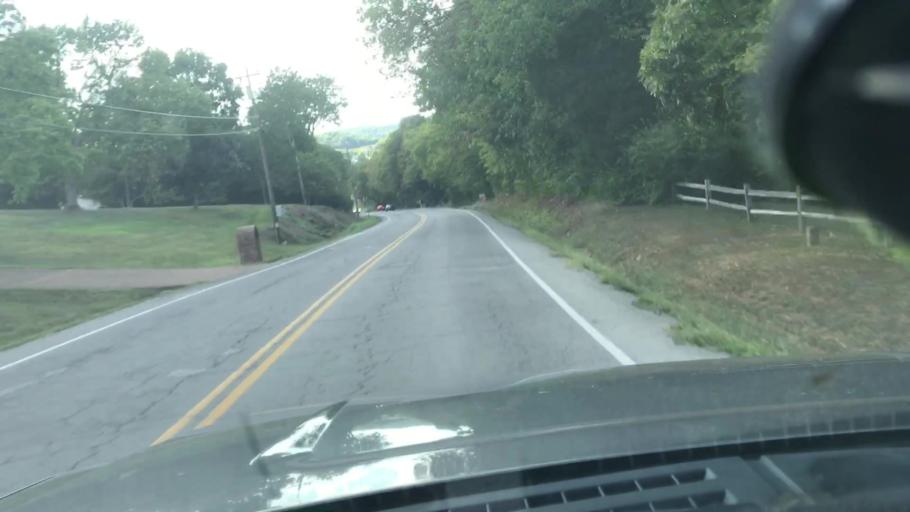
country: US
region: Tennessee
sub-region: Davidson County
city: Forest Hills
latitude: 36.0293
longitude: -86.9456
